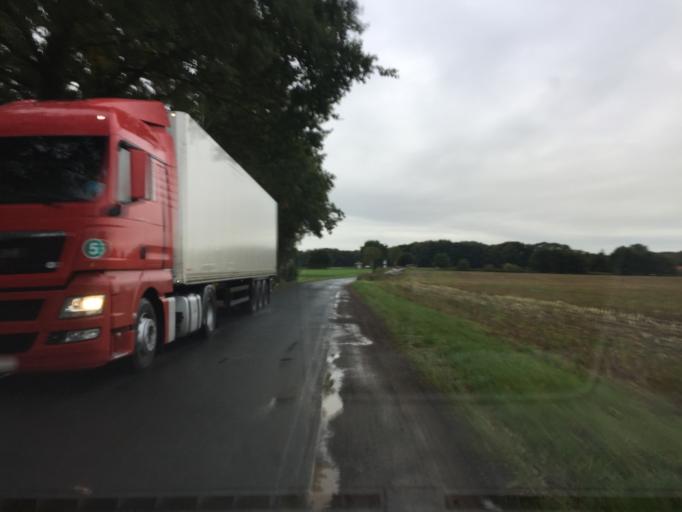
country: DE
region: Lower Saxony
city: Liebenau
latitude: 52.6416
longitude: 9.1028
